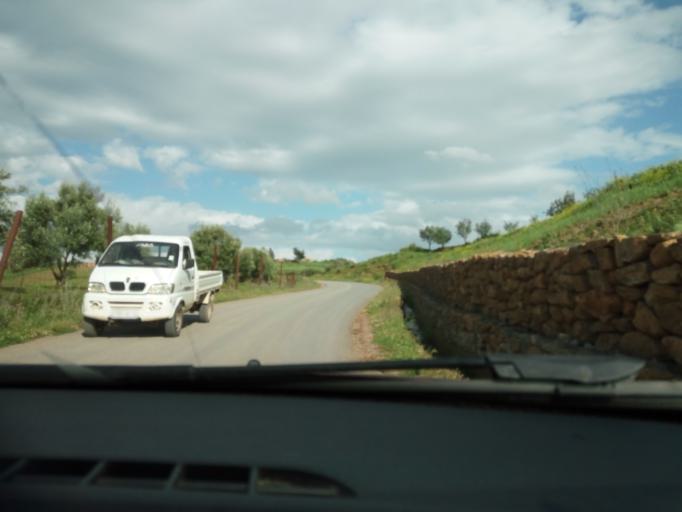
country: DZ
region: Tipaza
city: Hadjout
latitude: 36.3728
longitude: 2.4840
